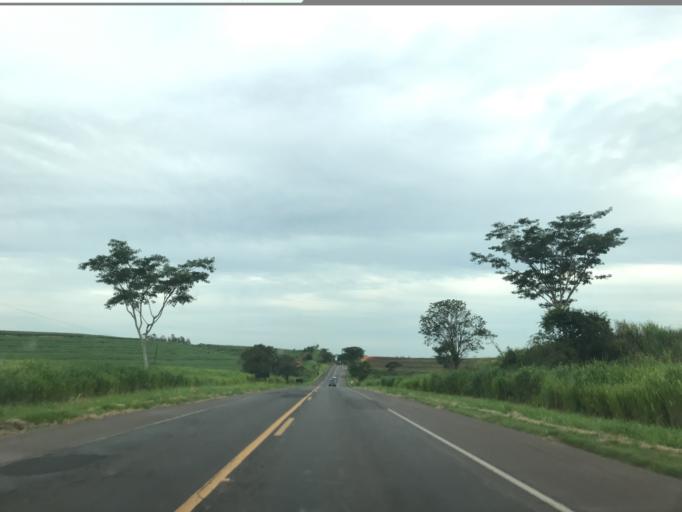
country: BR
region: Sao Paulo
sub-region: Birigui
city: Birigui
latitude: -21.5969
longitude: -50.4652
